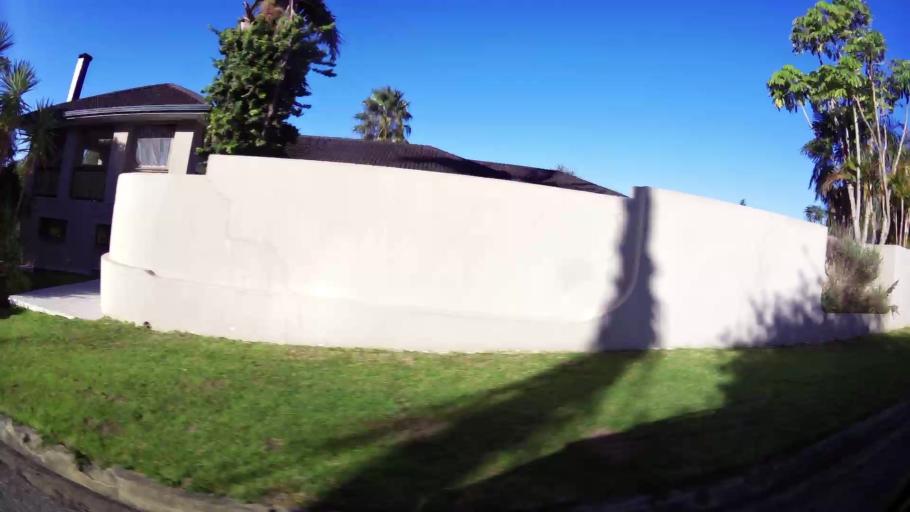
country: ZA
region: Western Cape
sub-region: Eden District Municipality
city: George
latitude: -33.9408
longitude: 22.4569
